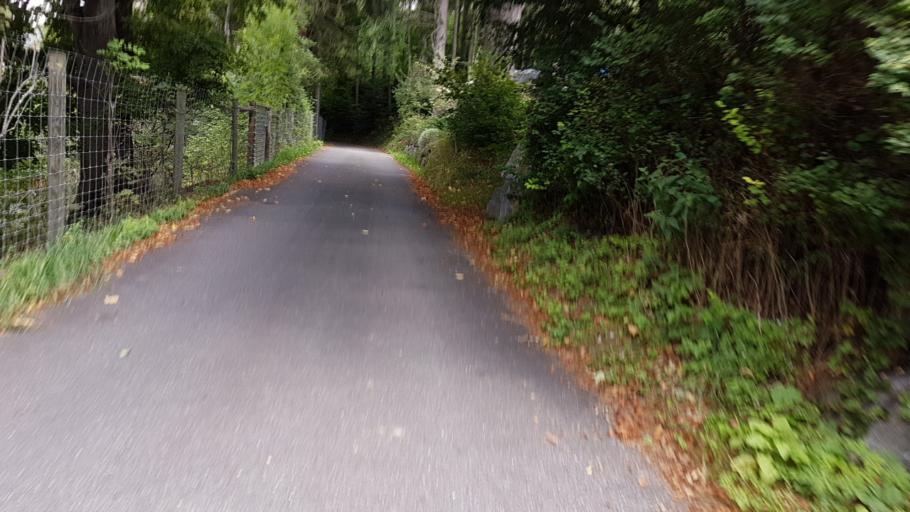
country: CH
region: Lucerne
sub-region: Entlebuch District
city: Oberdiessbach
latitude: 46.8219
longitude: 7.6374
